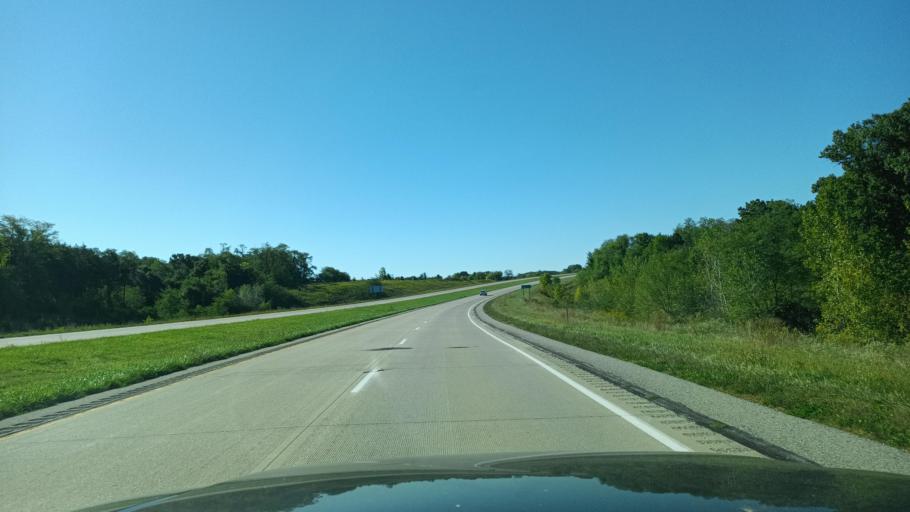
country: US
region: Iowa
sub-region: Lee County
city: Fort Madison
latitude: 40.6584
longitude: -91.3612
